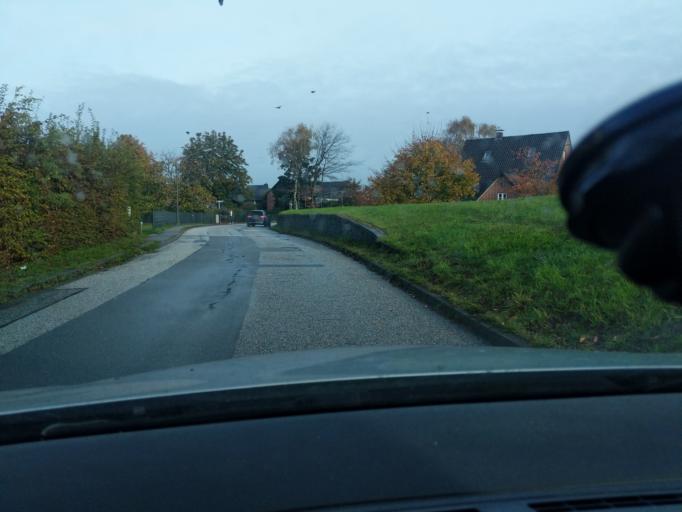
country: DE
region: Lower Saxony
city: Neu Wulmstorf
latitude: 53.5306
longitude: 9.7776
